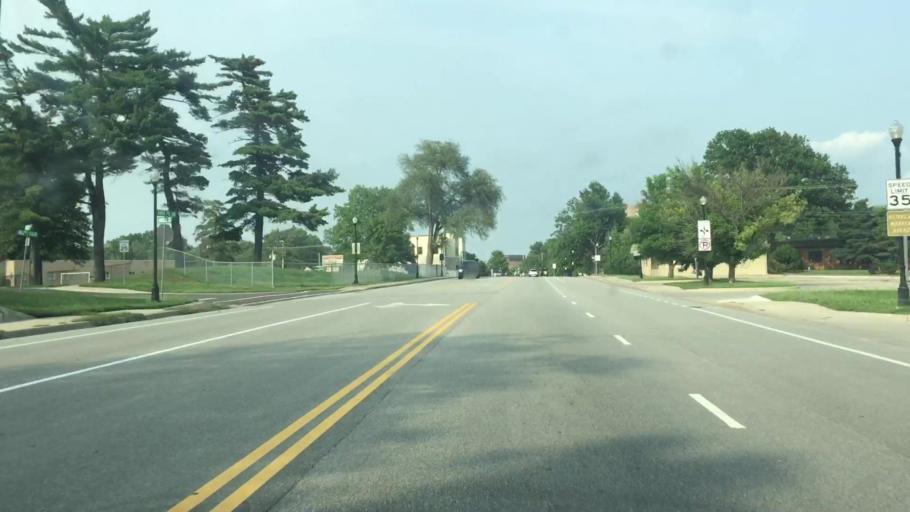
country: US
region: Kansas
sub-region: Johnson County
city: Overland Park
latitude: 38.9795
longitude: -94.6772
